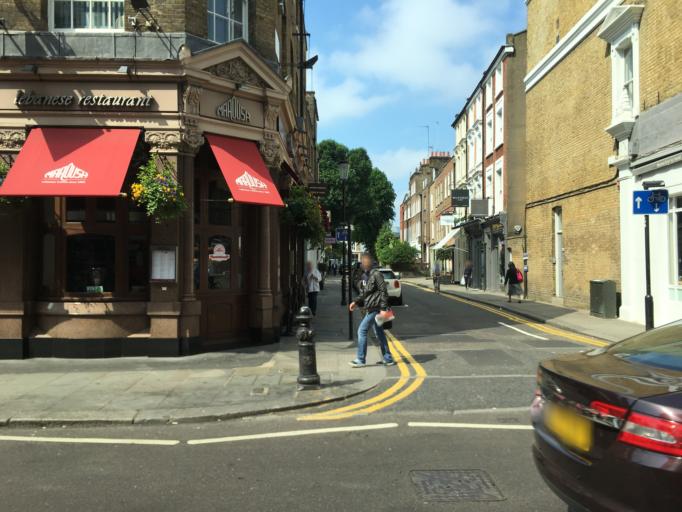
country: GB
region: England
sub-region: Greater London
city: Kensington
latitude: 51.5034
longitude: -0.1917
